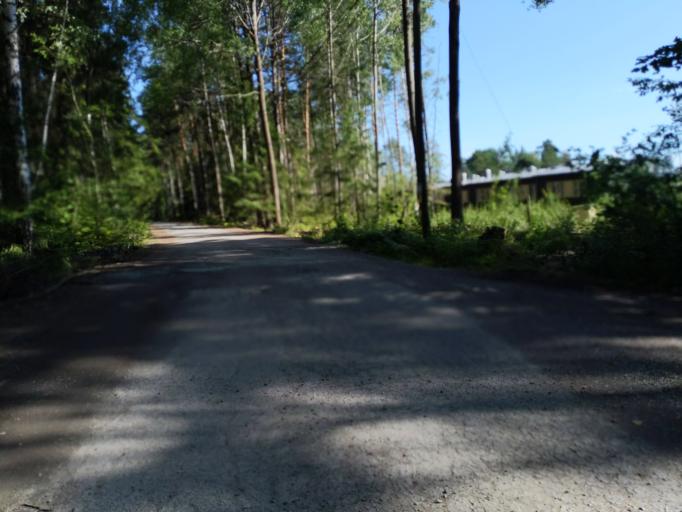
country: SE
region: Stockholm
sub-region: Solna Kommun
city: Rasunda
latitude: 59.3850
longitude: 17.9713
